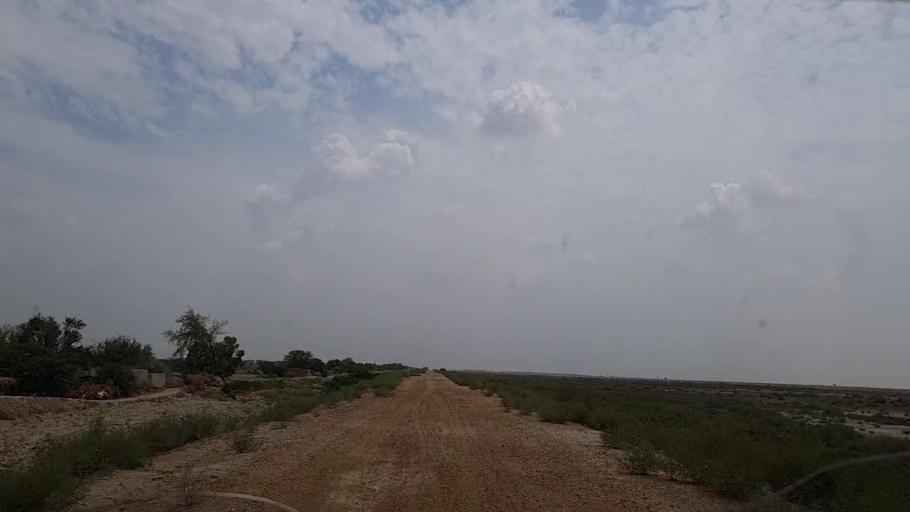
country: PK
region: Sindh
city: Johi
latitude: 26.7974
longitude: 67.6021
